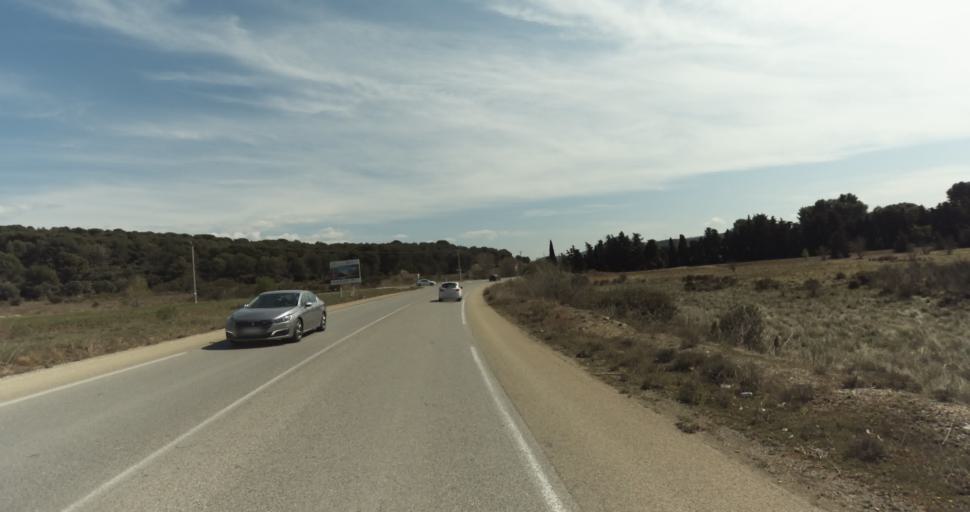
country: FR
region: Provence-Alpes-Cote d'Azur
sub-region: Departement des Bouches-du-Rhone
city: Coudoux
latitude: 43.5457
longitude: 5.2558
